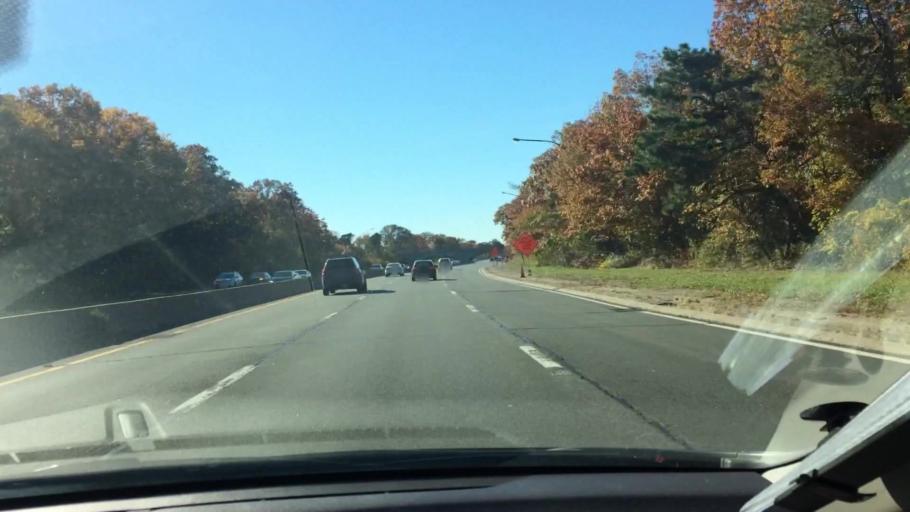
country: US
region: New York
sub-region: Suffolk County
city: North Lindenhurst
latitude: 40.7224
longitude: -73.3902
